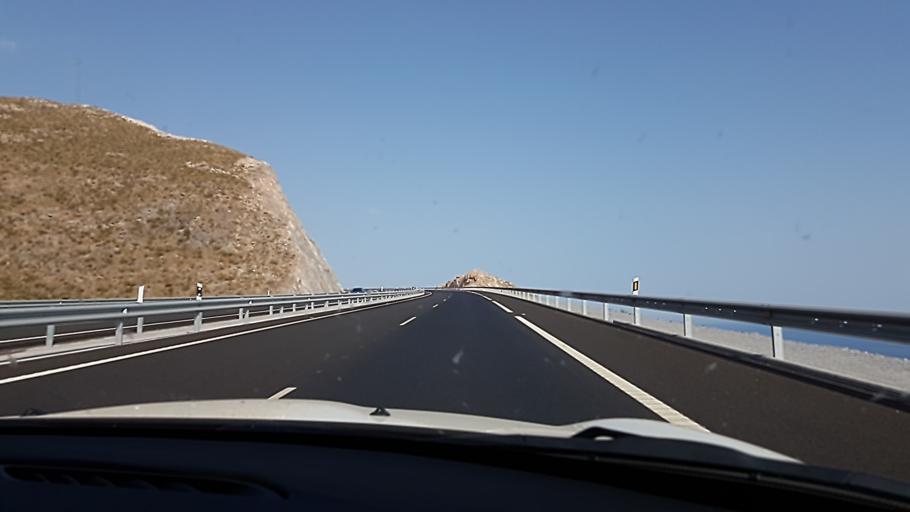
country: ES
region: Andalusia
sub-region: Provincia de Granada
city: Gualchos
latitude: 36.7153
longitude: -3.3908
